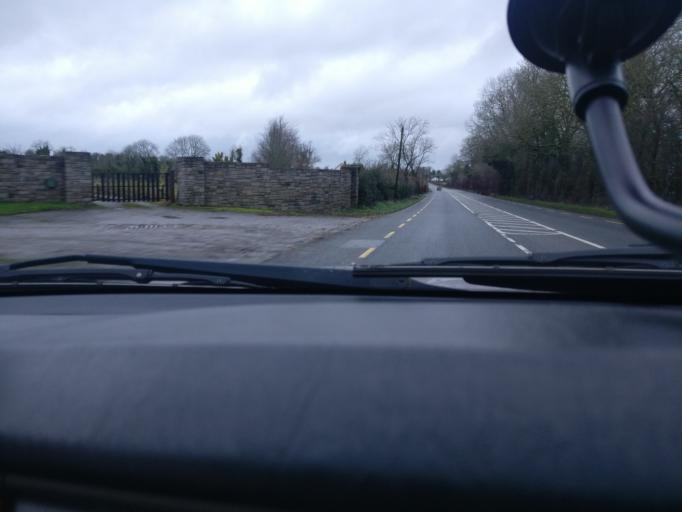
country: IE
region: Leinster
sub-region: Kildare
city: Kilcock
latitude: 53.4178
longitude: -6.7286
